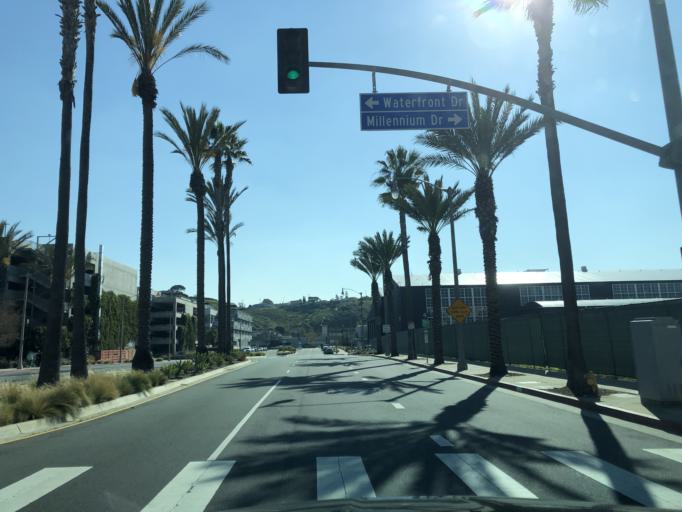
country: US
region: California
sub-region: Los Angeles County
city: Ladera Heights
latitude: 33.9796
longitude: -118.4080
